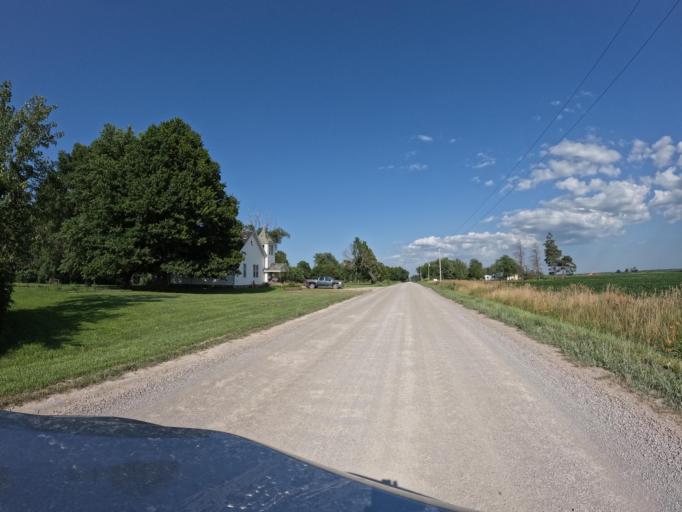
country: US
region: Iowa
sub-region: Appanoose County
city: Centerville
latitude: 40.7175
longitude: -93.0332
